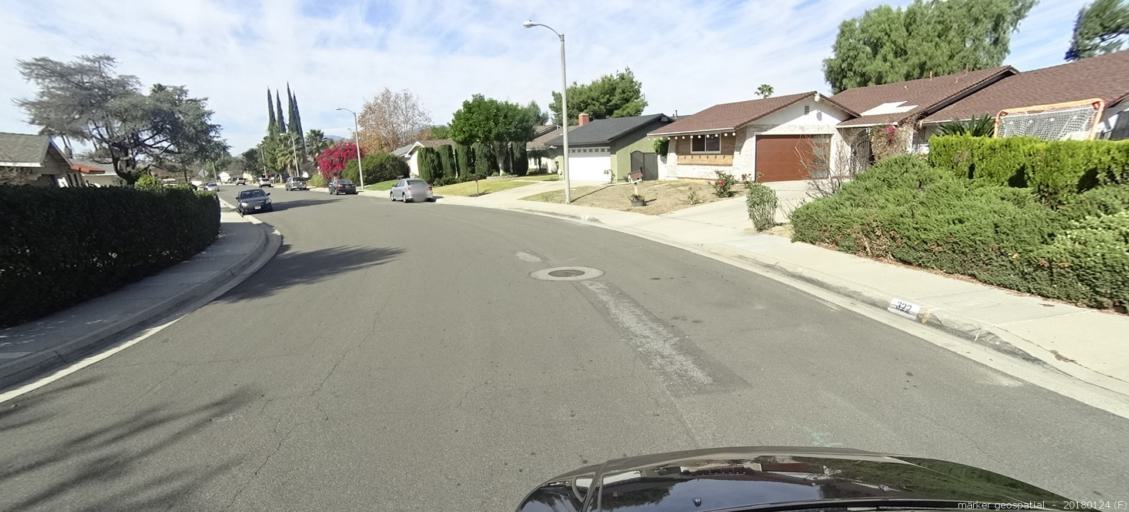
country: US
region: California
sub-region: Los Angeles County
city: Diamond Bar
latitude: 34.0275
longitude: -117.8134
